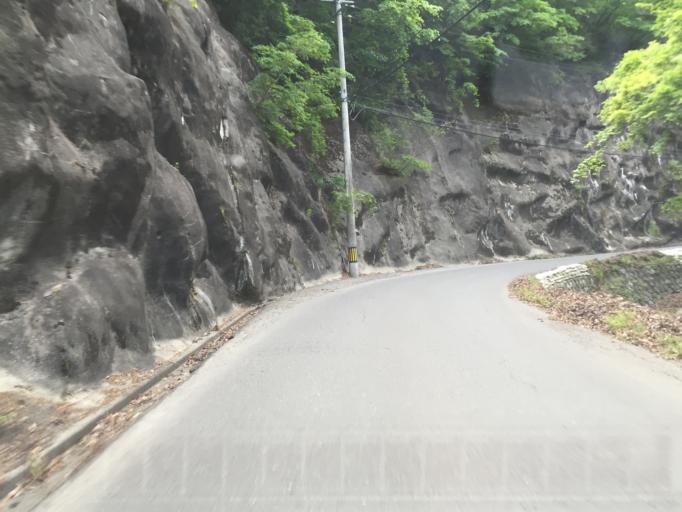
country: JP
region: Fukushima
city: Yanagawamachi-saiwaicho
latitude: 37.8967
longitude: 140.6661
